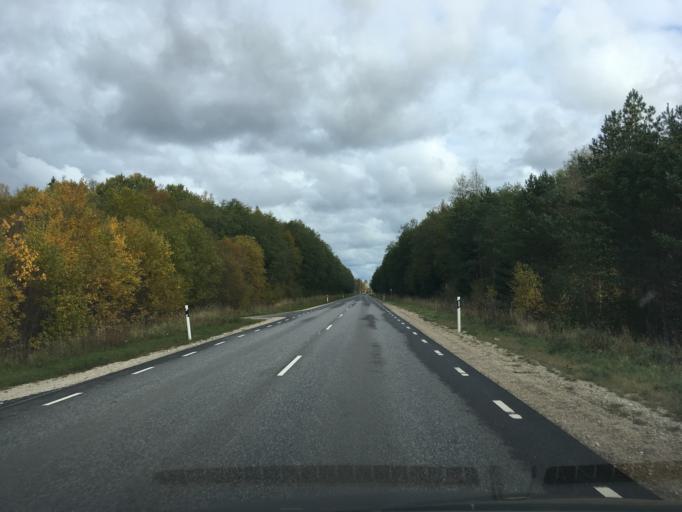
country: EE
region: Harju
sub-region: Anija vald
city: Kehra
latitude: 59.2394
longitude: 25.2929
